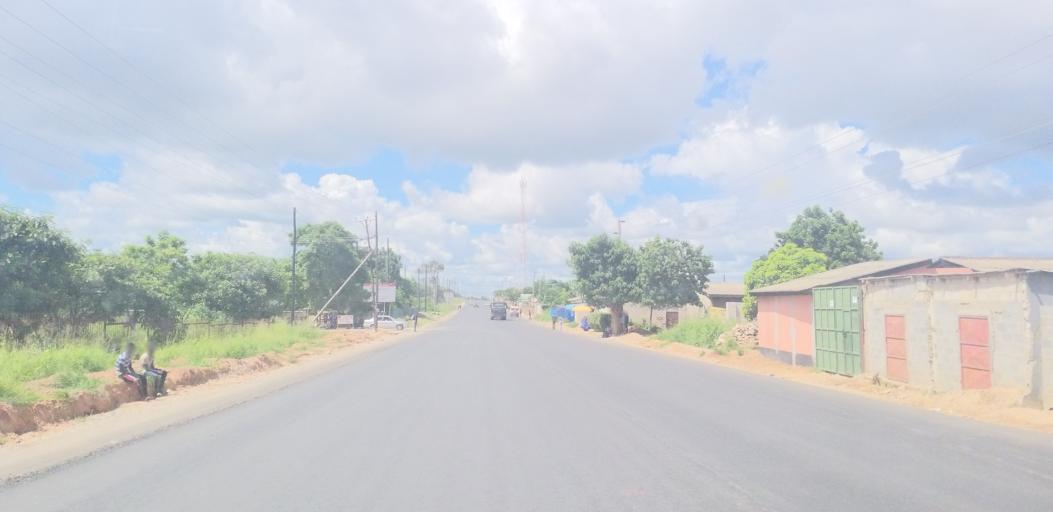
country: ZM
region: Lusaka
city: Lusaka
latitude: -15.3626
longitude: 28.3214
